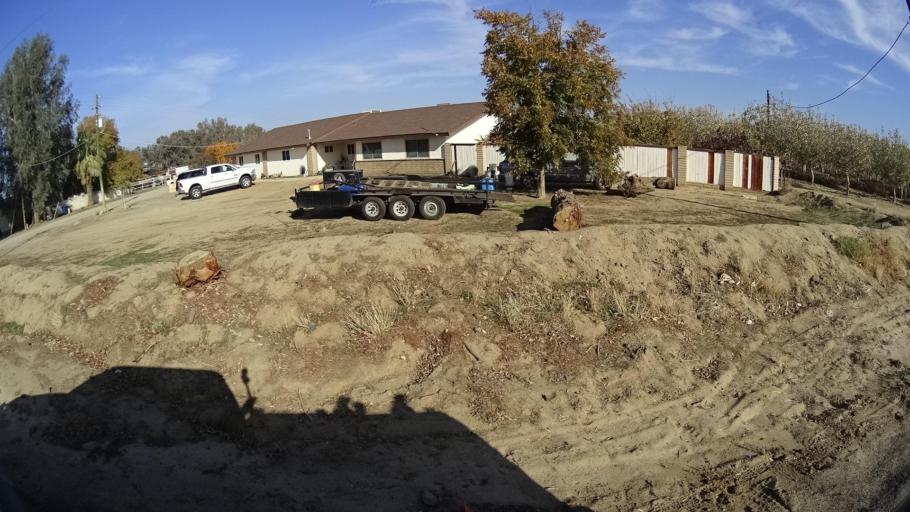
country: US
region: California
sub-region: Kern County
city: Lamont
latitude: 35.3253
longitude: -118.9099
